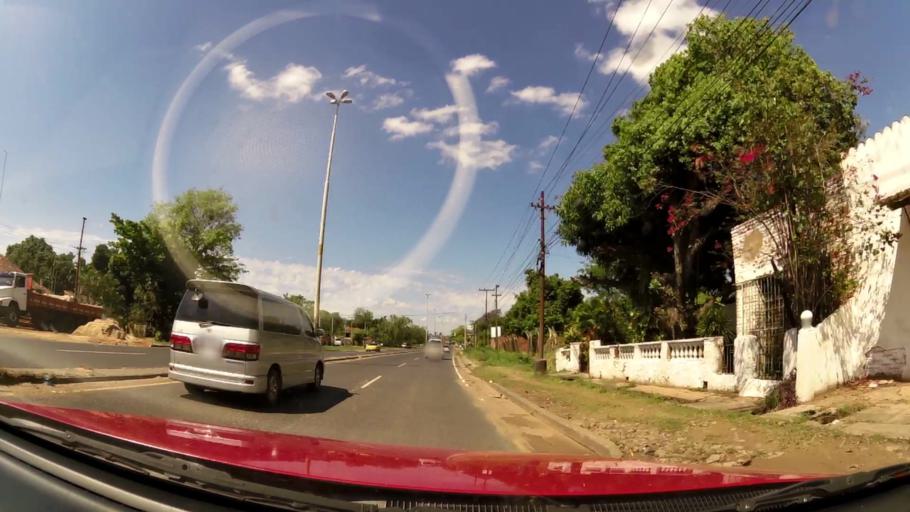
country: PY
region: Central
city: Colonia Mariano Roque Alonso
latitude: -25.2520
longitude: -57.5575
